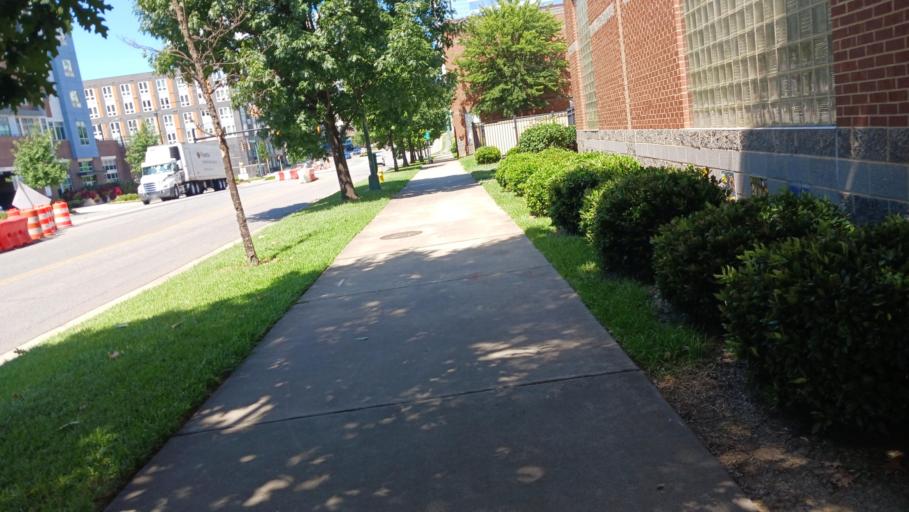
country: US
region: North Carolina
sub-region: Mecklenburg County
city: Charlotte
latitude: 35.2183
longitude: -80.8426
